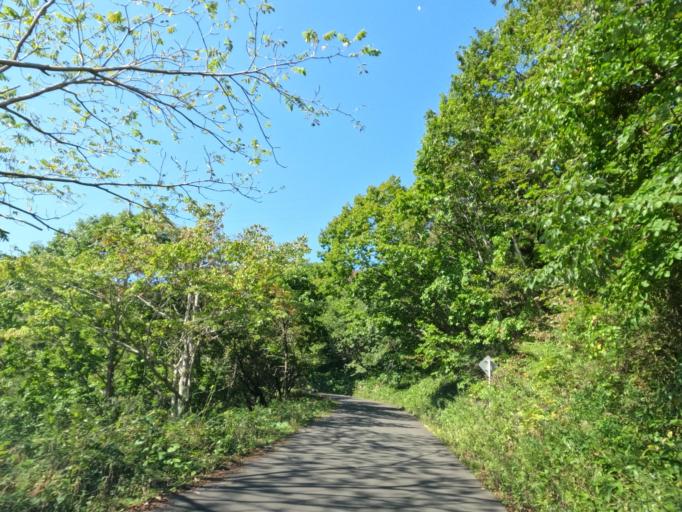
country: JP
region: Hokkaido
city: Muroran
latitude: 42.3660
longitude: 141.0207
